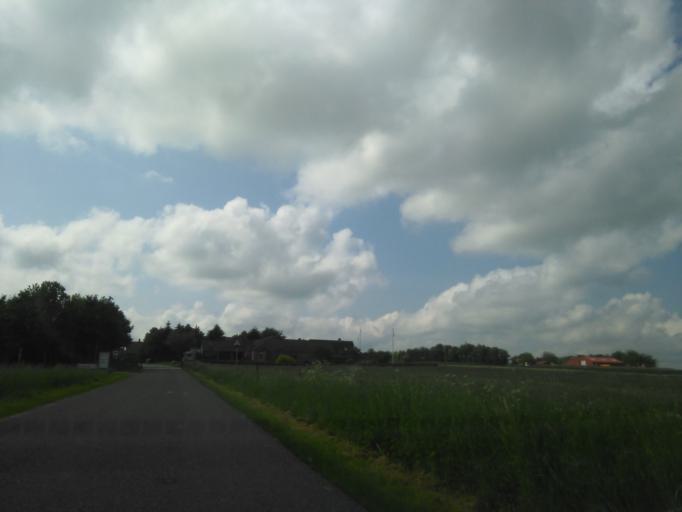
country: DK
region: Central Jutland
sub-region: Skanderborg Kommune
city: Skovby
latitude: 56.2033
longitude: 9.9682
